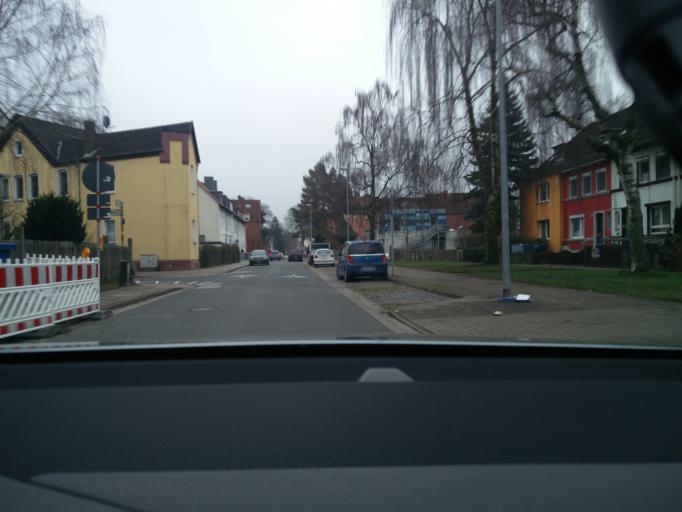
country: DE
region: Lower Saxony
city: Laatzen
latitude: 52.3306
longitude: 9.7718
